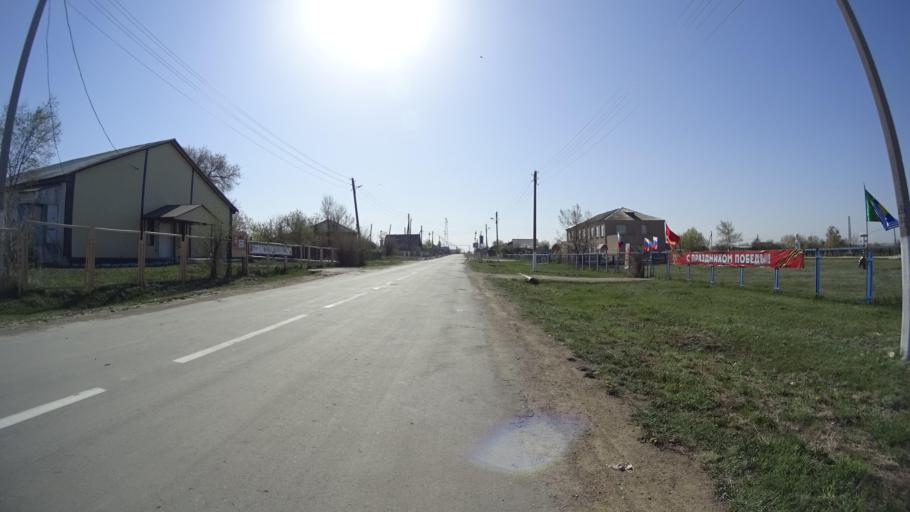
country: RU
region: Chelyabinsk
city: Chesma
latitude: 53.7963
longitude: 61.0290
